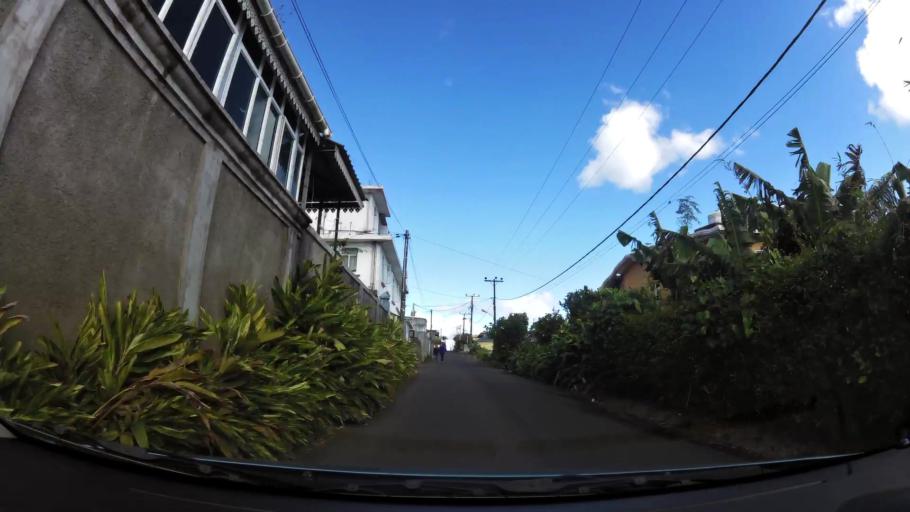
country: MU
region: Plaines Wilhems
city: Curepipe
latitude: -20.3048
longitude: 57.5102
